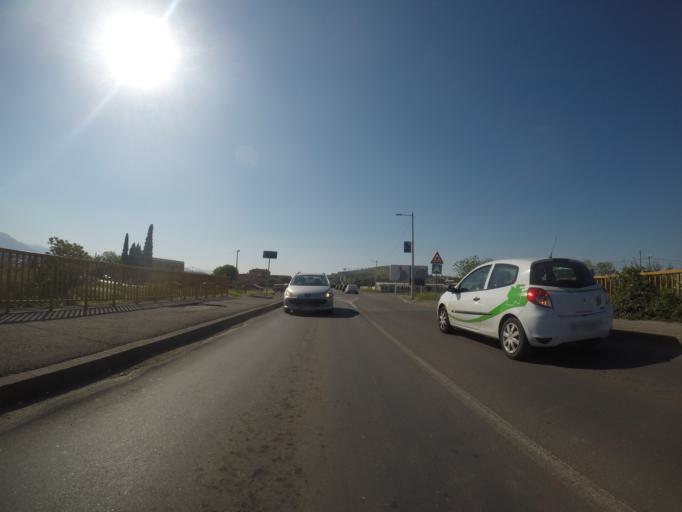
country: ME
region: Podgorica
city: Podgorica
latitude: 42.4336
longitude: 19.2292
